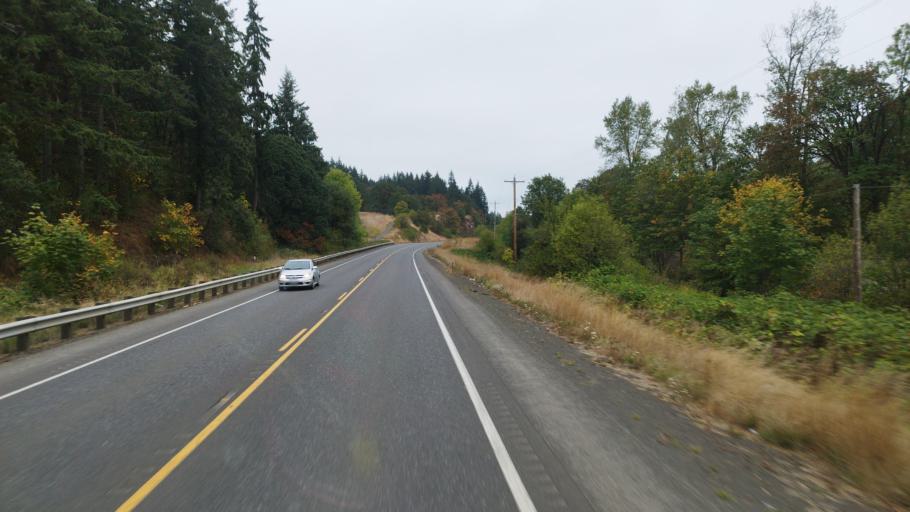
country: US
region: Washington
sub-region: Cowlitz County
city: Kalama
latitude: 45.9678
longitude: -122.8680
